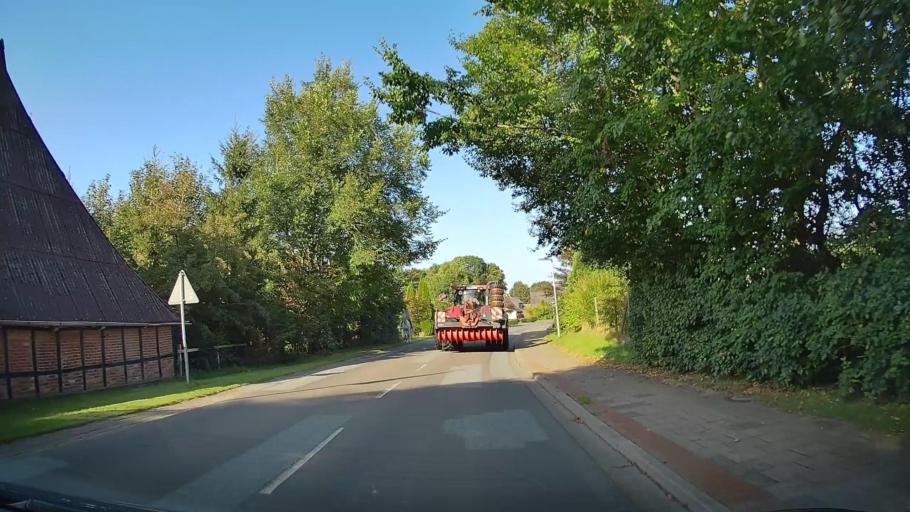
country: DE
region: Lower Saxony
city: Nordholz
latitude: 53.7749
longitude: 8.5884
